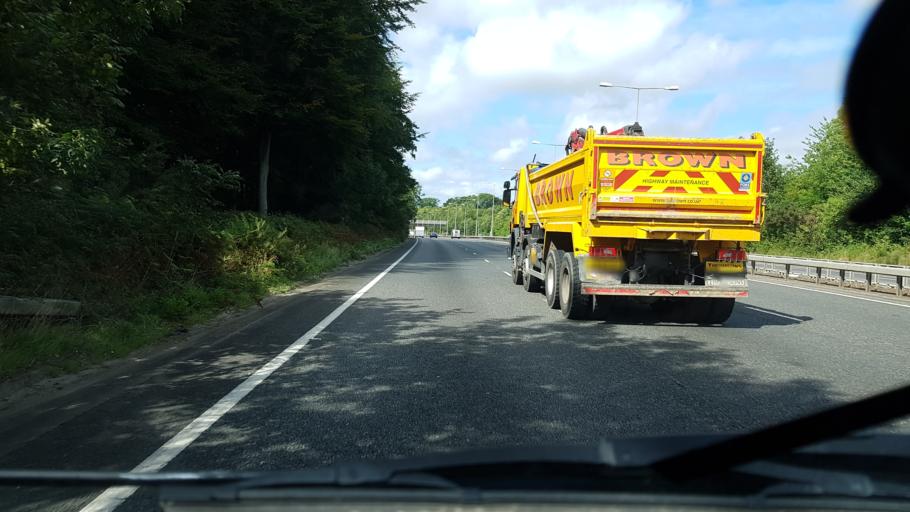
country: GB
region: England
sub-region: West Sussex
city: Broadfield
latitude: 51.0562
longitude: -0.2025
